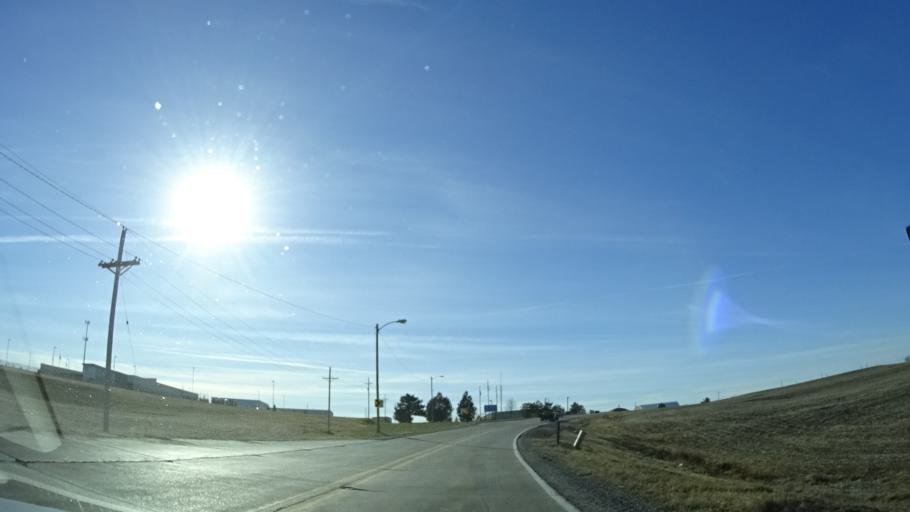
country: US
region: Nebraska
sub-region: Sarpy County
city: Papillion
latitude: 41.0918
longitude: -96.0431
